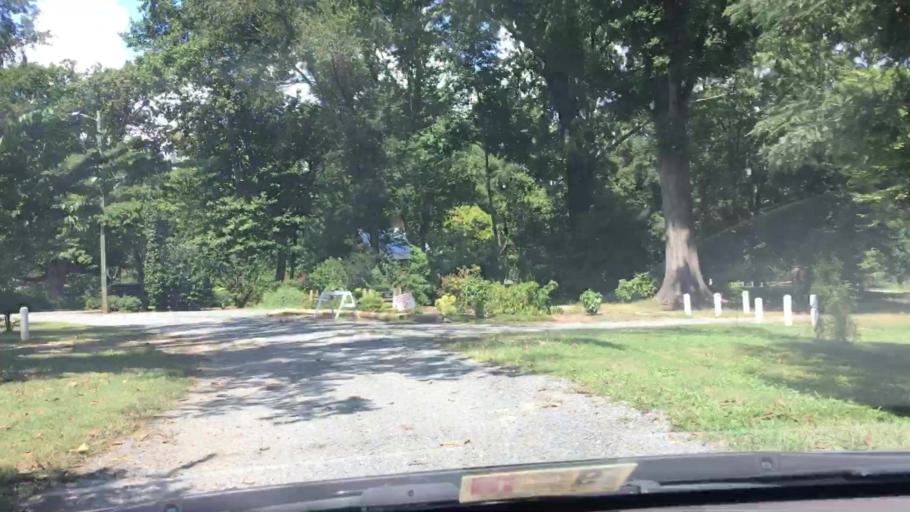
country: US
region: North Carolina
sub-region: Mecklenburg County
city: Charlotte
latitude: 35.2545
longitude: -80.8052
